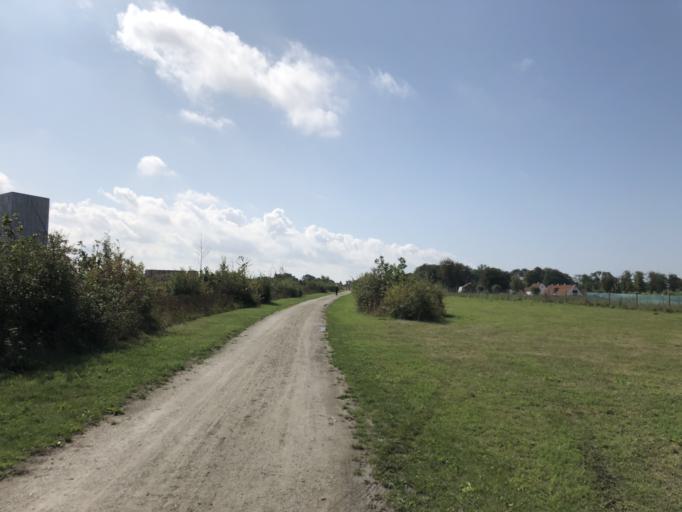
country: SE
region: Skane
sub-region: Malmo
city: Bunkeflostrand
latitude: 55.5523
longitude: 12.9787
